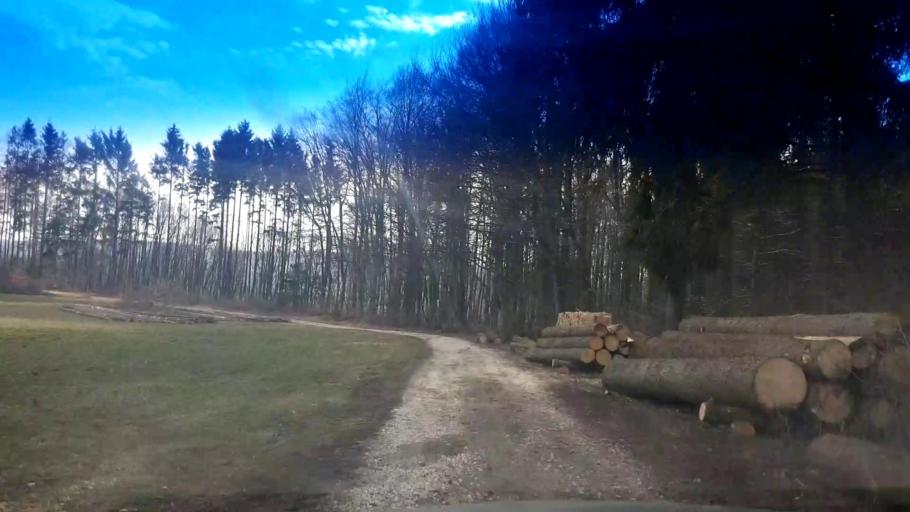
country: DE
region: Bavaria
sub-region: Upper Franconia
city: Litzendorf
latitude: 49.9285
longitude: 11.0618
